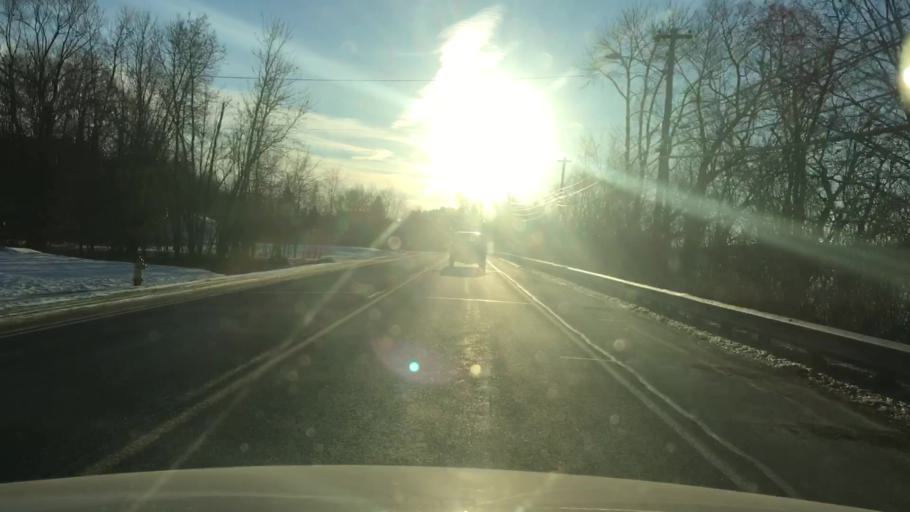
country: US
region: Maine
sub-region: Penobscot County
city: Brewer
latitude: 44.8136
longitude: -68.7319
